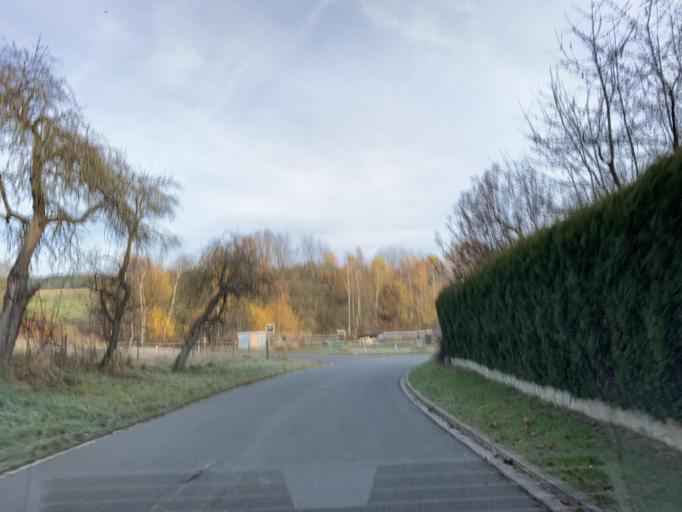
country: DE
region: Bavaria
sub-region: Upper Palatinate
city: Neukirchen-Balbini
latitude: 49.3360
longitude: 12.4396
